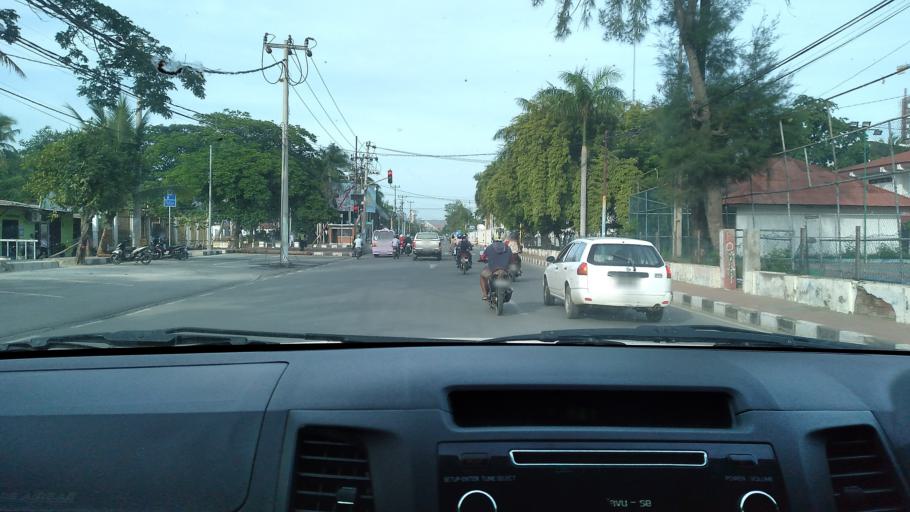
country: TL
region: Dili
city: Dili
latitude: -8.5568
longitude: 125.5767
